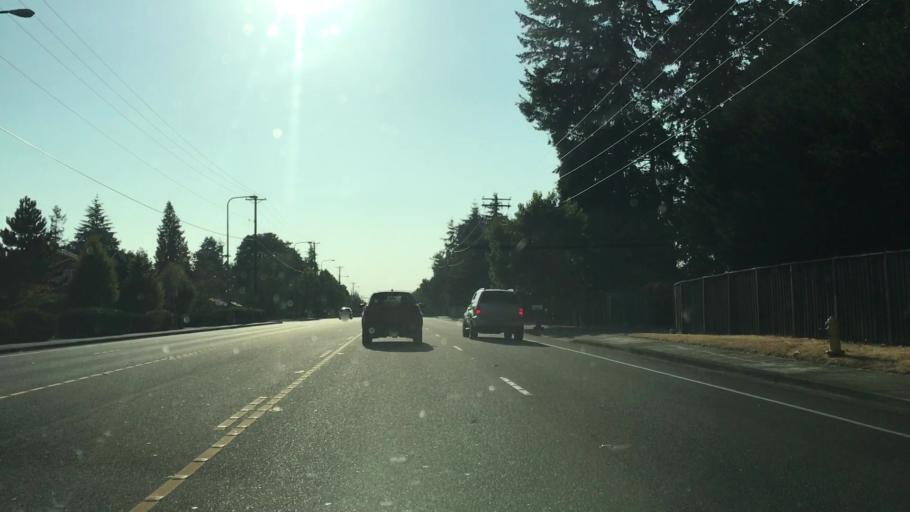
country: US
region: Washington
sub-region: Pierce County
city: Fife Heights
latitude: 47.2826
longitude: -122.3562
